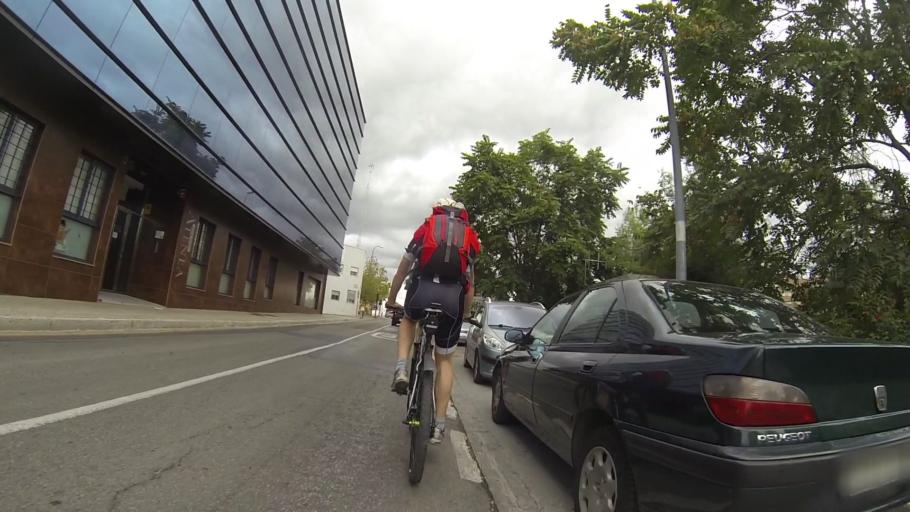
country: ES
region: Andalusia
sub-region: Provincia de Granada
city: Granada
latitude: 37.1952
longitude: -3.6214
